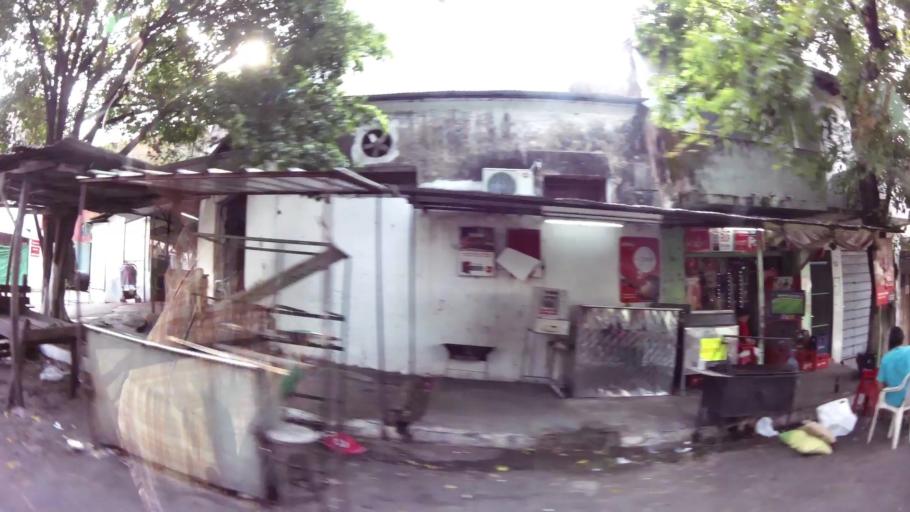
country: PY
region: Asuncion
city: Asuncion
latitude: -25.2977
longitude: -57.6211
